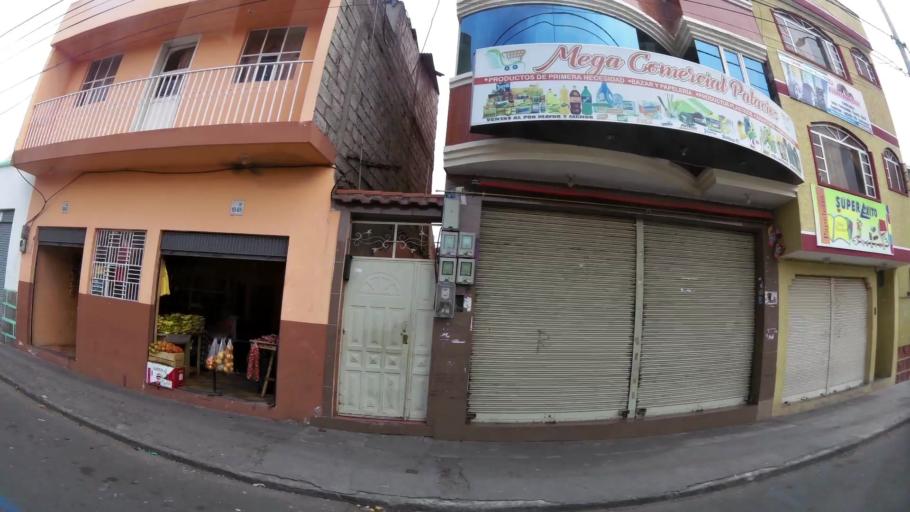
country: EC
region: Cotopaxi
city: Latacunga
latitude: -0.9299
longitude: -78.6125
